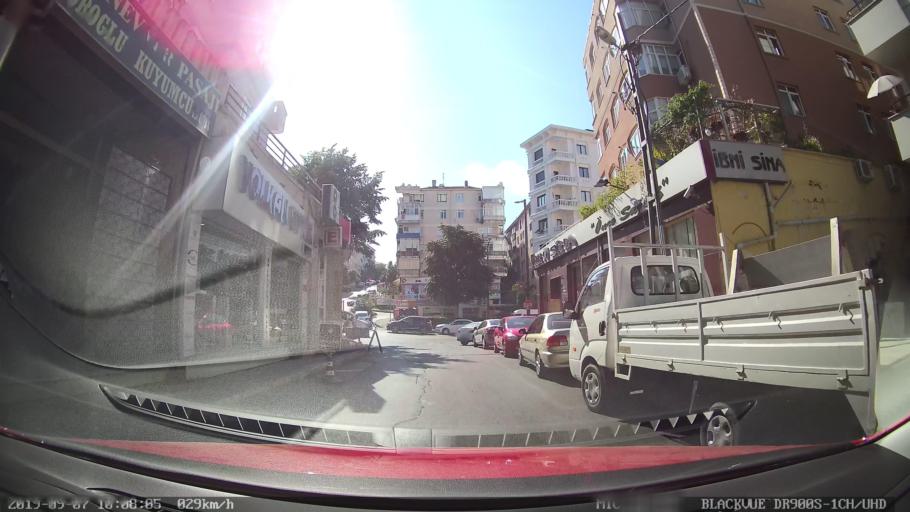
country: TR
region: Istanbul
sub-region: Atasehir
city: Atasehir
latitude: 40.9481
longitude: 29.1129
